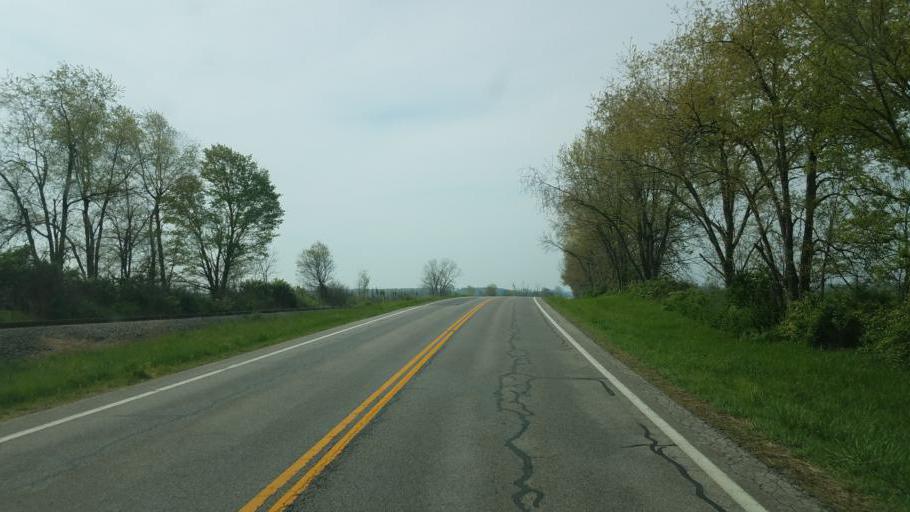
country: US
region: Ohio
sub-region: Licking County
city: Utica
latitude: 40.2842
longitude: -82.4492
